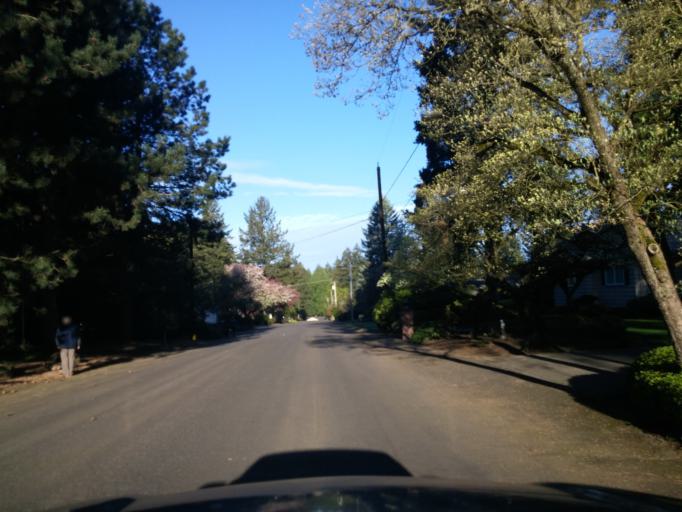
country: US
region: Oregon
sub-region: Washington County
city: Cedar Hills
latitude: 45.5013
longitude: -122.7816
